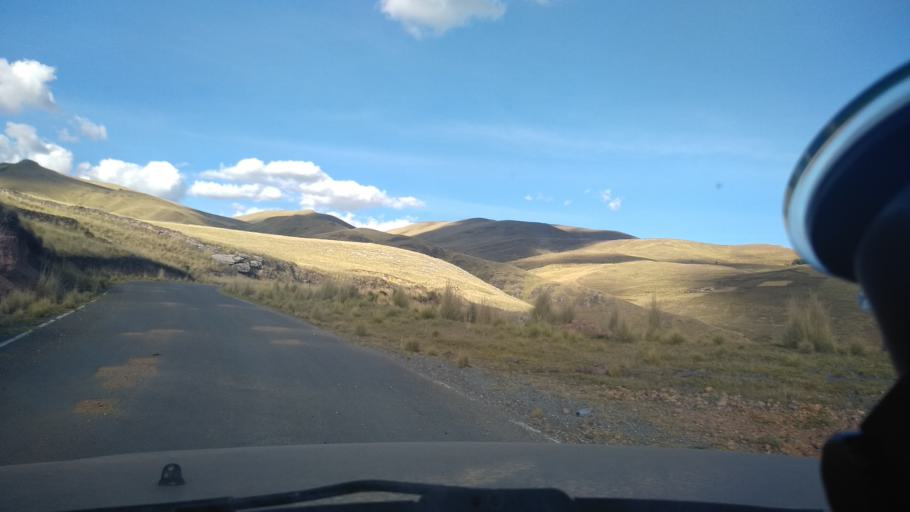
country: PE
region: Cusco
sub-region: Provincia de Canas
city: Cahuanuyo
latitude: -14.3420
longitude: -71.4486
